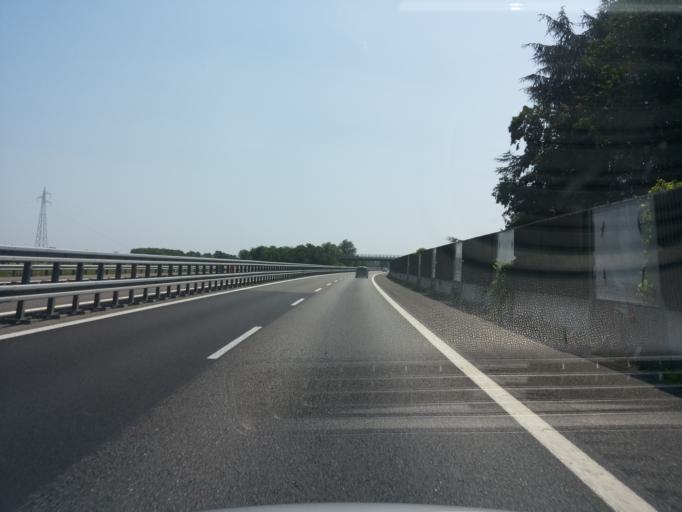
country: IT
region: Lombardy
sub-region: Provincia di Pavia
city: Zerbo
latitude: 45.0849
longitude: 9.3921
